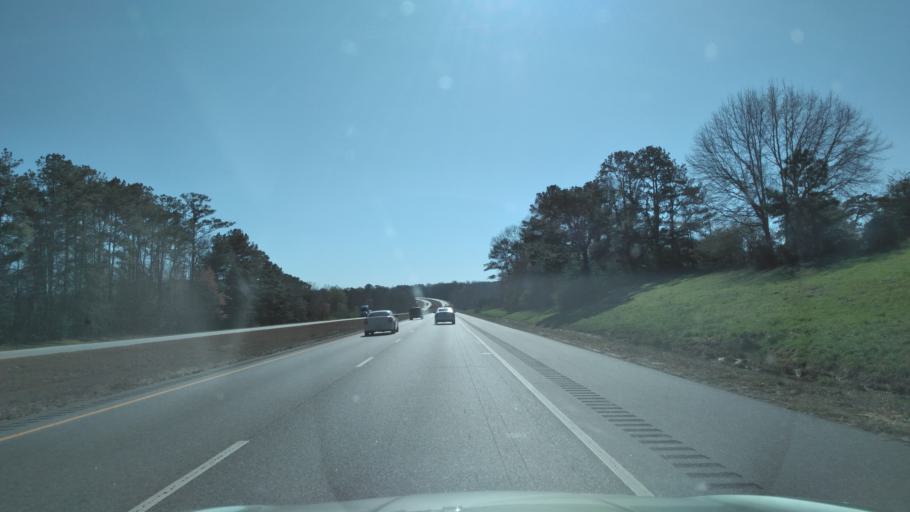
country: US
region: Alabama
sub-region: Lowndes County
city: Fort Deposit
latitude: 31.9510
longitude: -86.5529
